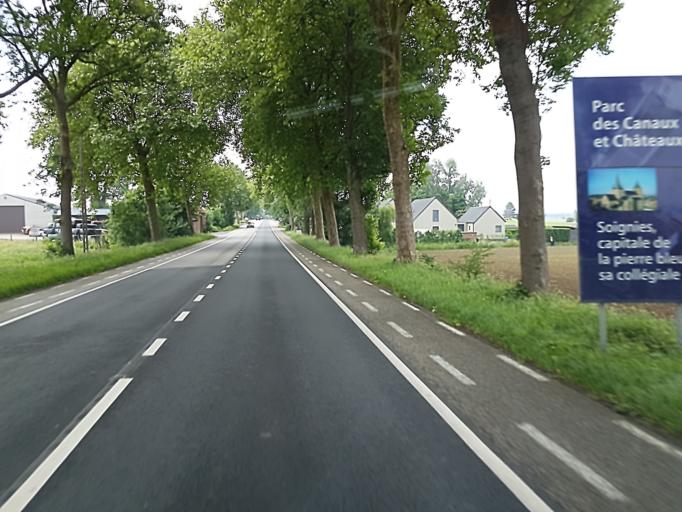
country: BE
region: Wallonia
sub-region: Province du Hainaut
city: Soignies
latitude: 50.6065
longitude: 4.0580
